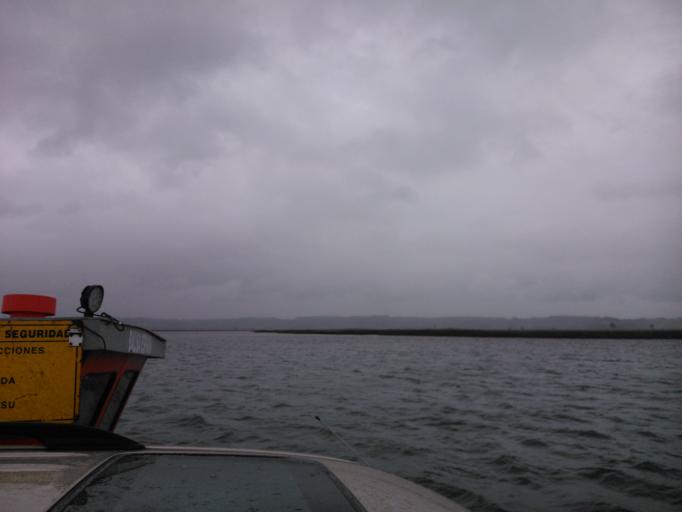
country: CL
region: Araucania
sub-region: Provincia de Cautin
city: Carahue
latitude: -38.7489
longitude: -73.4082
